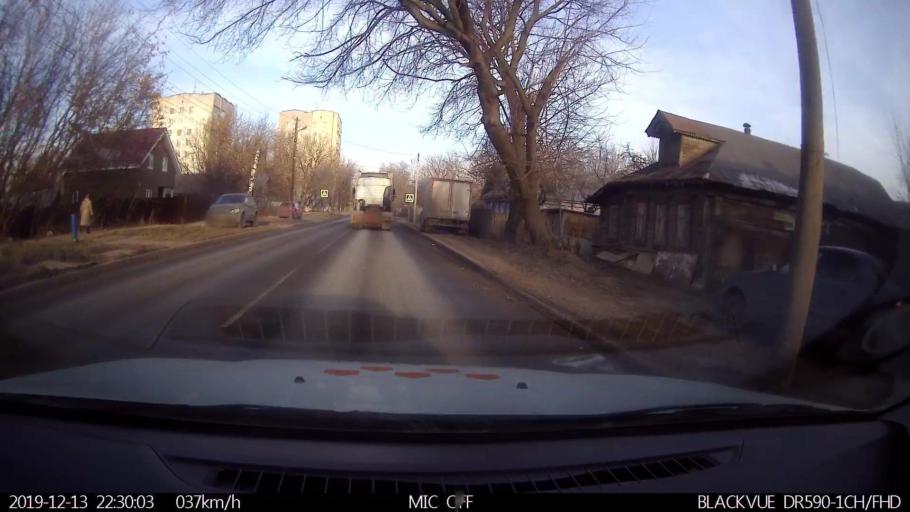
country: RU
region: Nizjnij Novgorod
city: Nizhniy Novgorod
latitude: 56.2771
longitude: 43.9512
